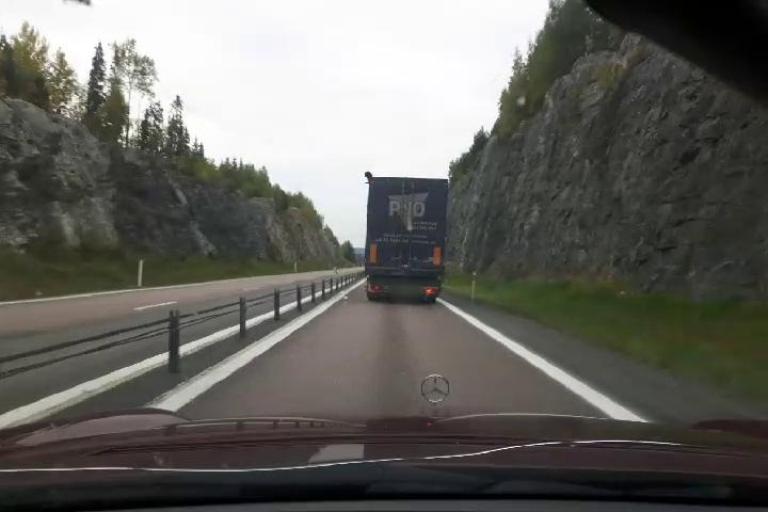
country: SE
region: Vaesternorrland
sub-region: Haernoesands Kommun
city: Haernoesand
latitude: 62.8287
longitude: 17.9681
